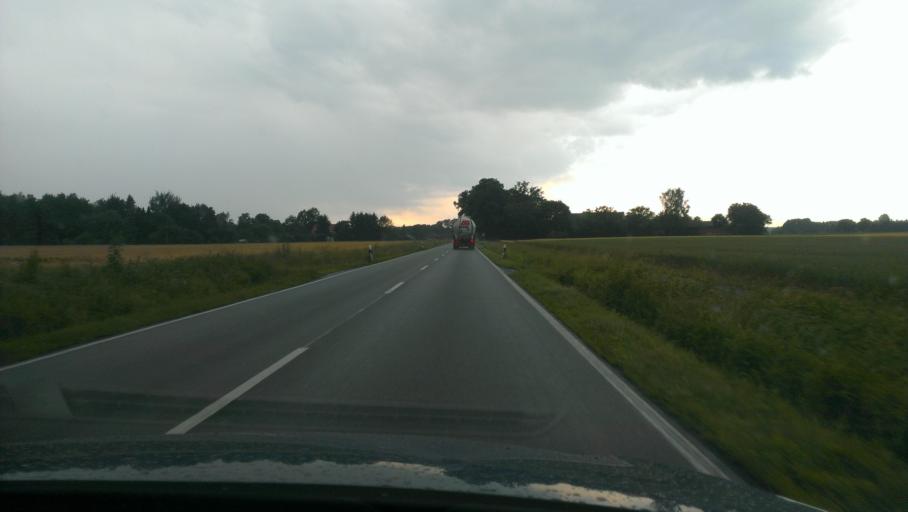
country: DE
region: North Rhine-Westphalia
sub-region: Regierungsbezirk Munster
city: Drensteinfurt
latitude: 51.8843
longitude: 7.7171
